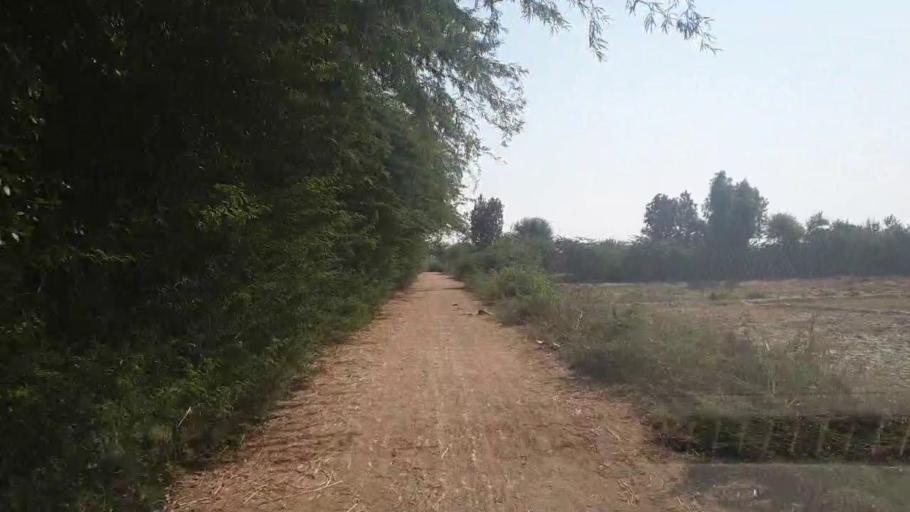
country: PK
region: Sindh
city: Badin
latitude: 24.6801
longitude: 68.8691
